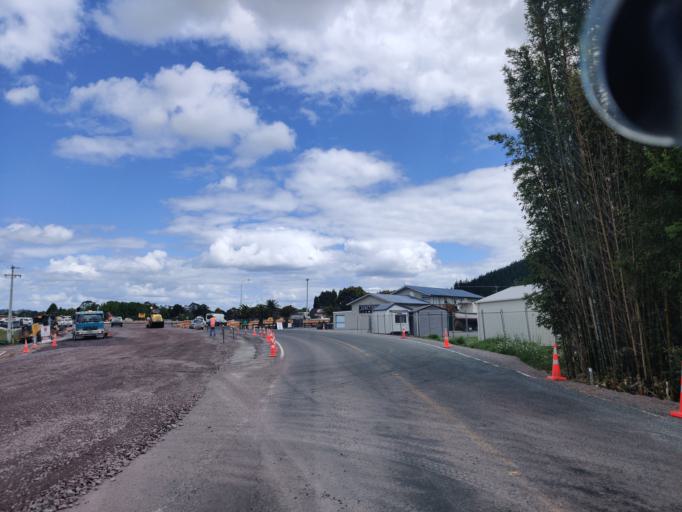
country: NZ
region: Northland
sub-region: Far North District
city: Kerikeri
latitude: -35.3019
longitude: 173.9620
